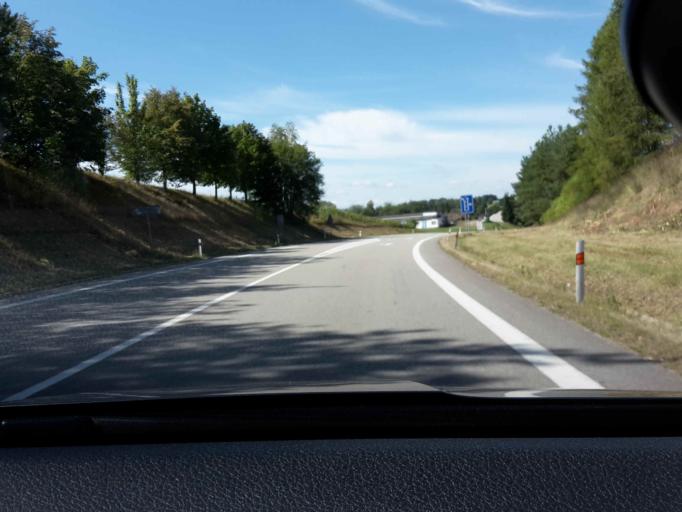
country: CZ
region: Jihocesky
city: Strmilov
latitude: 49.1547
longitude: 15.1992
